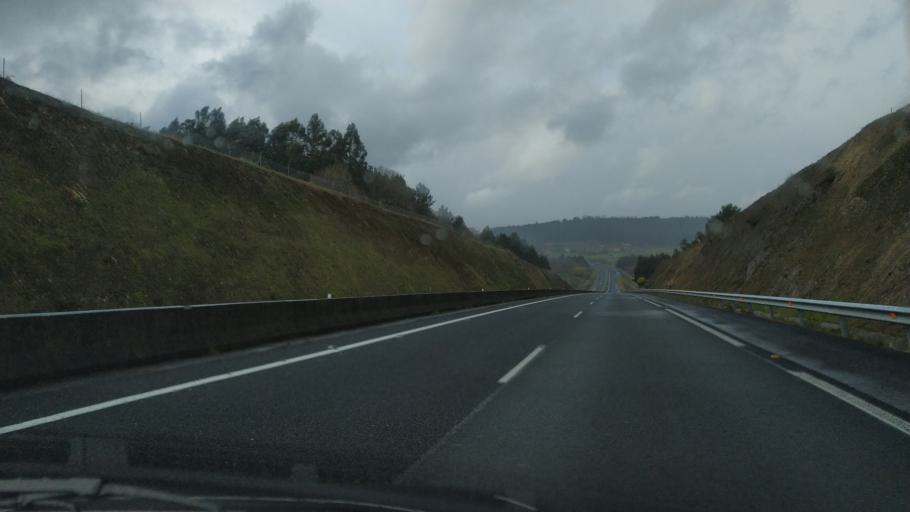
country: ES
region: Galicia
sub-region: Provincia de Pontevedra
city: Silleda
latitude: 42.7219
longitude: -8.3133
